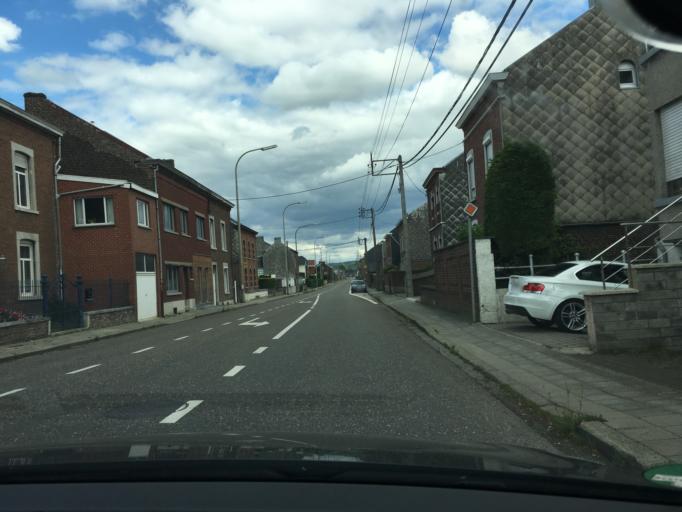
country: BE
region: Wallonia
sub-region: Province de Liege
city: Amay
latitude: 50.5402
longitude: 5.2919
